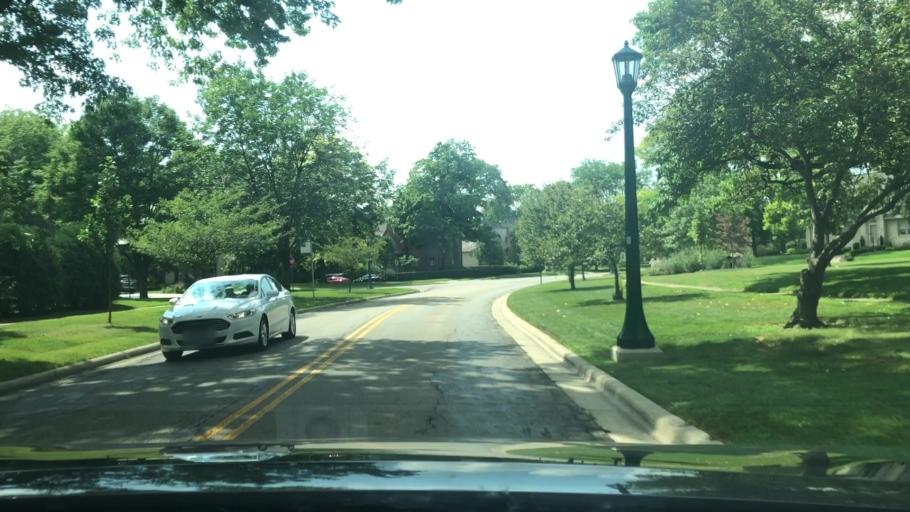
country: US
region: Ohio
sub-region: Franklin County
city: Upper Arlington
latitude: 40.0025
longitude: -83.0657
